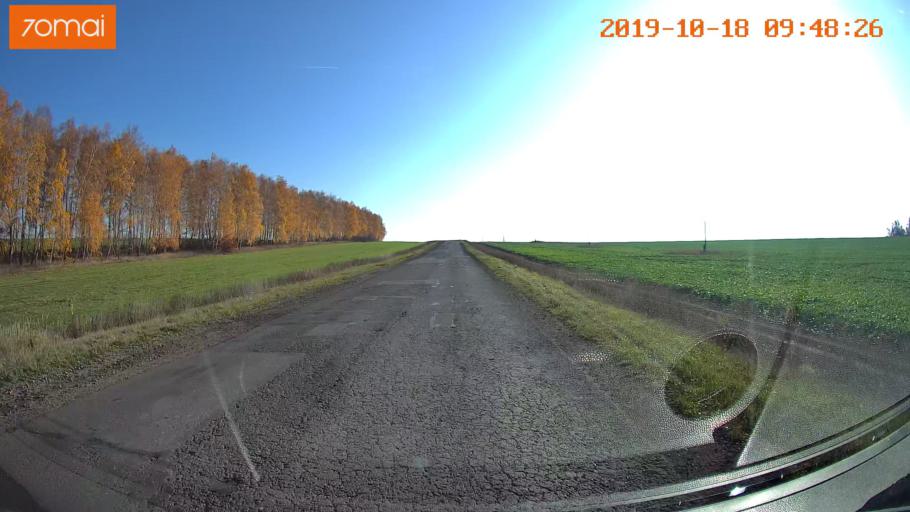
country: RU
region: Tula
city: Kazachka
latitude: 53.3179
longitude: 38.2495
